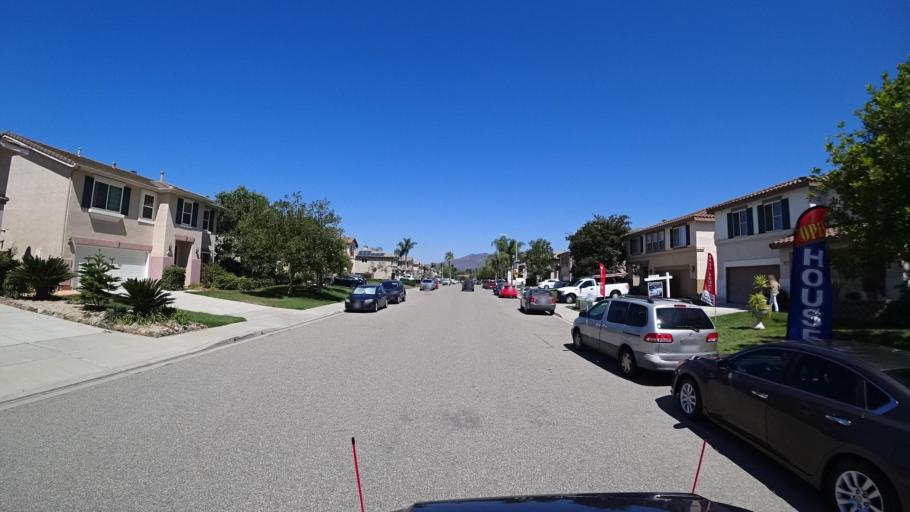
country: US
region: California
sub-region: San Diego County
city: Bonsall
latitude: 33.3227
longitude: -117.1485
